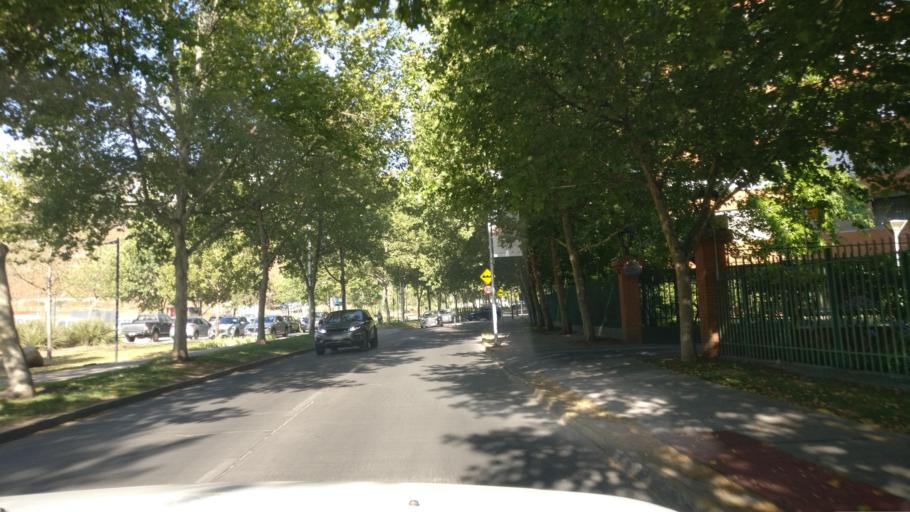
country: CL
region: Santiago Metropolitan
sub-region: Provincia de Santiago
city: Villa Presidente Frei, Nunoa, Santiago, Chile
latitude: -33.3759
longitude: -70.5497
